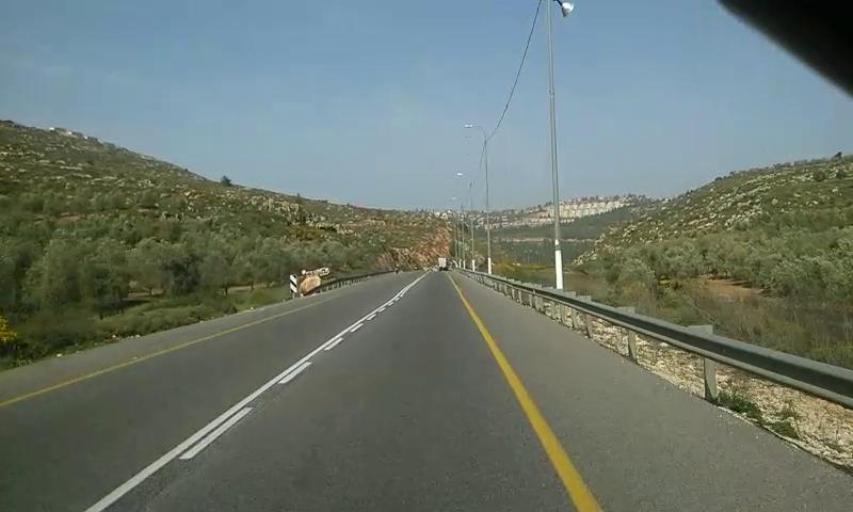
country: PS
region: West Bank
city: Qaryut
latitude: 32.0635
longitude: 35.2764
